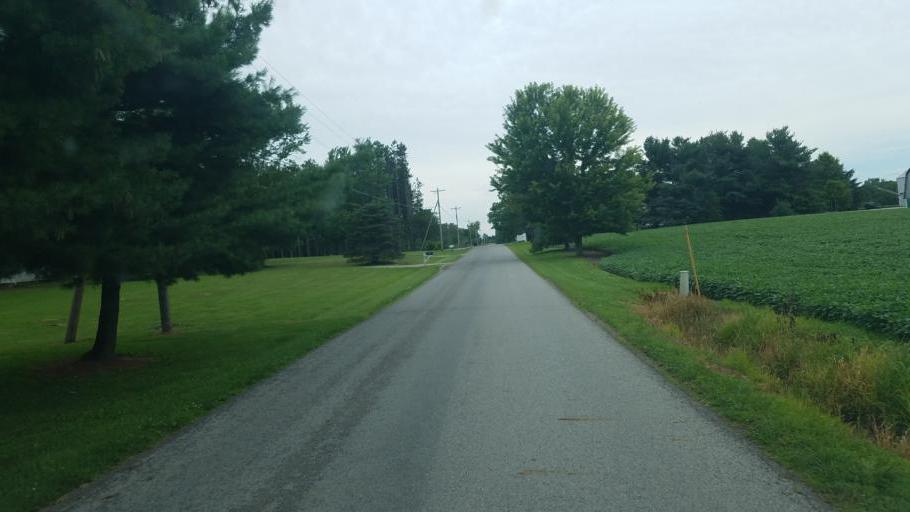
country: US
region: Ohio
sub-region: Licking County
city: Johnstown
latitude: 40.2140
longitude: -82.5886
